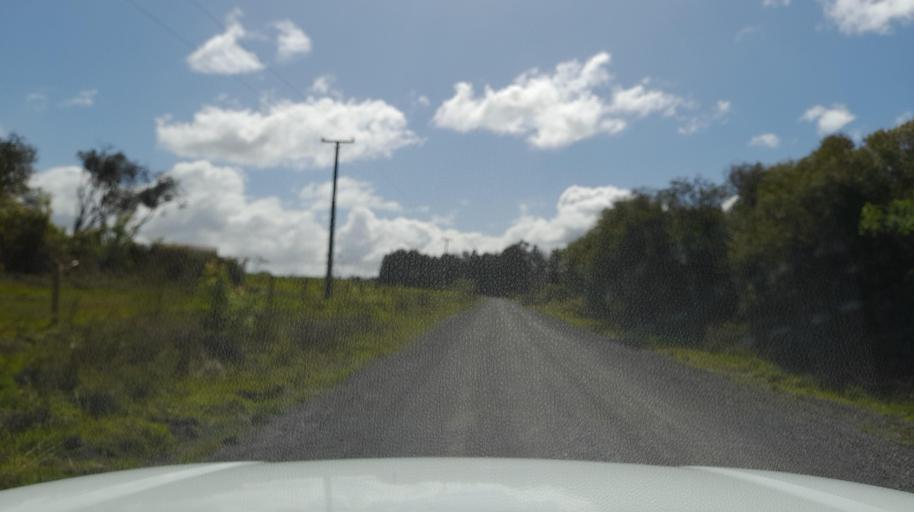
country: NZ
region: Northland
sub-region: Far North District
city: Kerikeri
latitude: -35.2280
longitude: 173.8760
